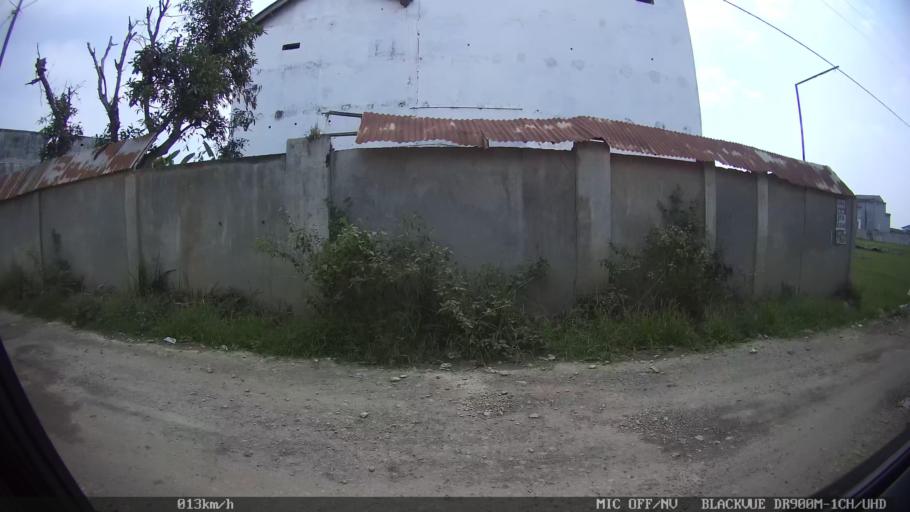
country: ID
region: Lampung
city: Gadingrejo
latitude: -5.3744
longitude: 105.0301
